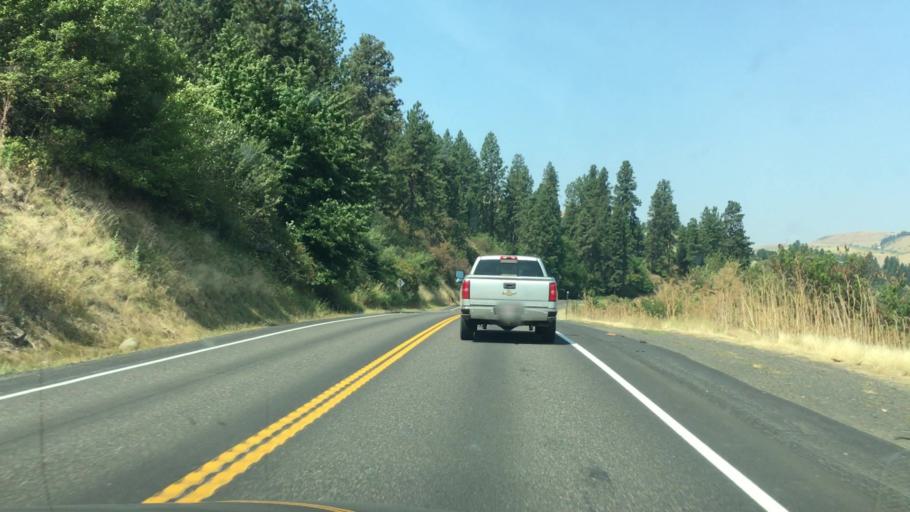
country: US
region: Idaho
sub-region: Clearwater County
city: Orofino
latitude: 46.5000
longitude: -116.4977
